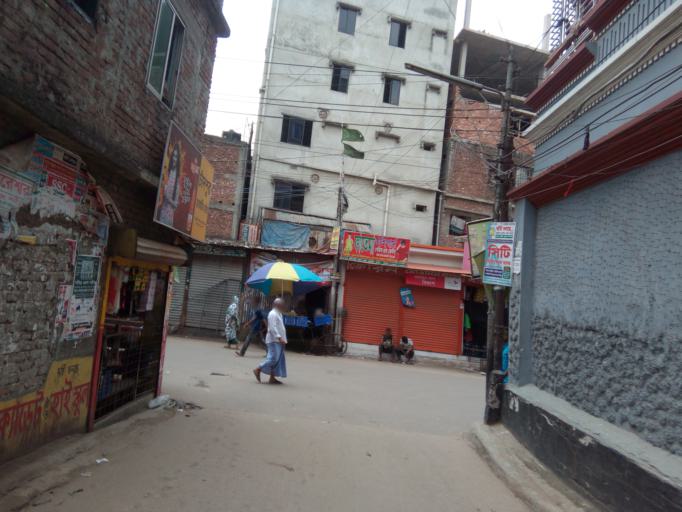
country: BD
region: Dhaka
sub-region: Dhaka
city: Dhaka
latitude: 23.6983
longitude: 90.4317
